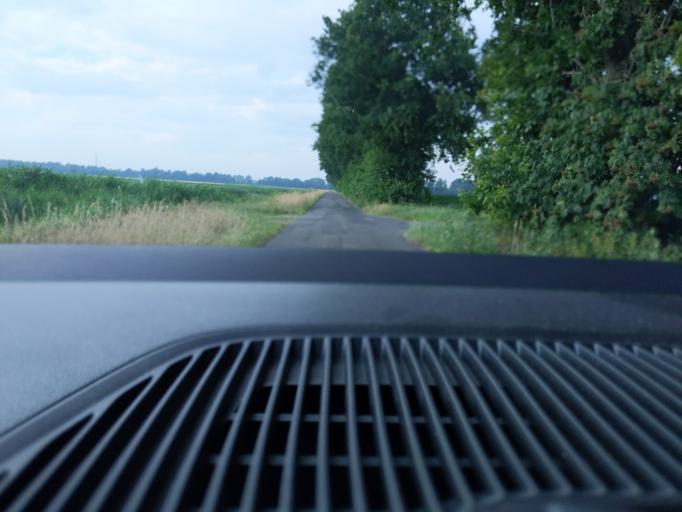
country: NL
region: Drenthe
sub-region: Gemeente Emmen
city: Emmer-Compascuum
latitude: 52.7702
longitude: 7.1031
